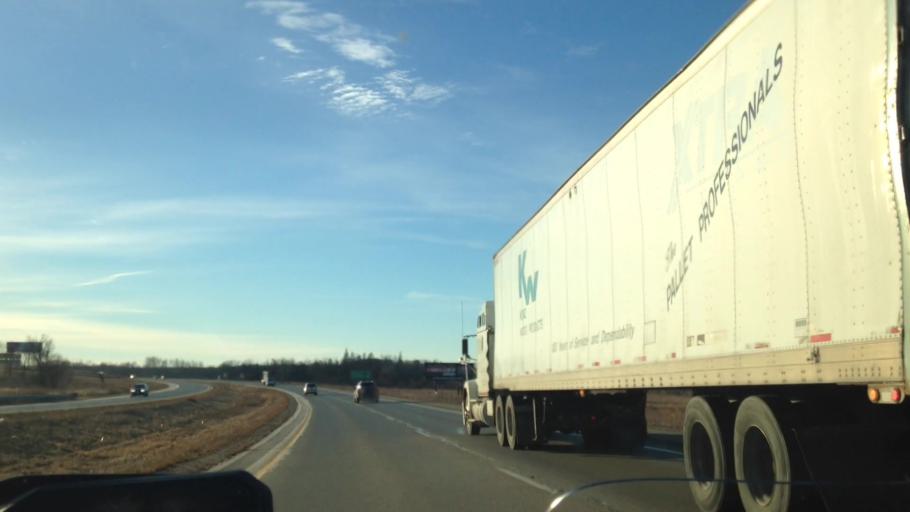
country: US
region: Wisconsin
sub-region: Dodge County
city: Theresa
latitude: 43.4630
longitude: -88.3668
